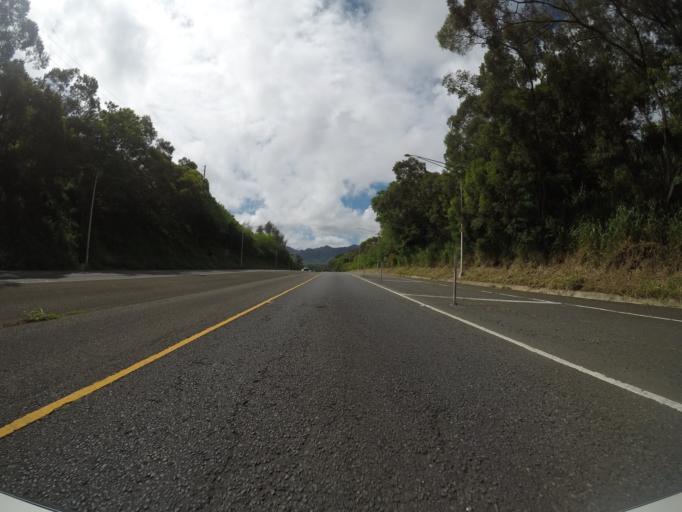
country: US
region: Hawaii
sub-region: Honolulu County
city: Waimanalo
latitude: 21.3597
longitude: -157.7345
